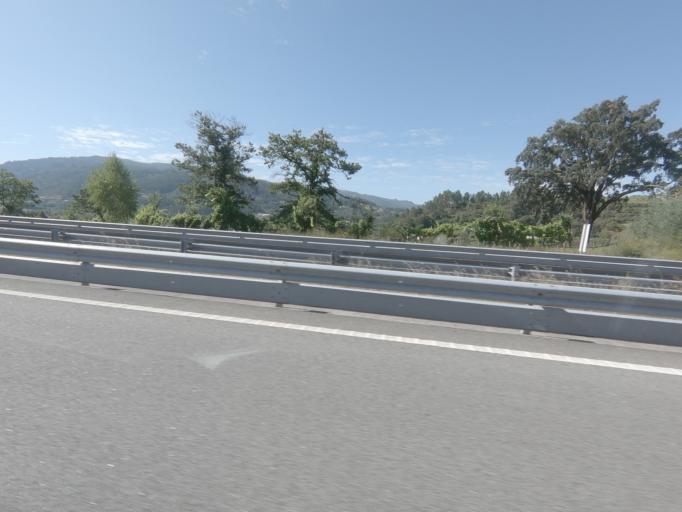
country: PT
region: Porto
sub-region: Amarante
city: Amarante
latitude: 41.2587
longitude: -8.0546
